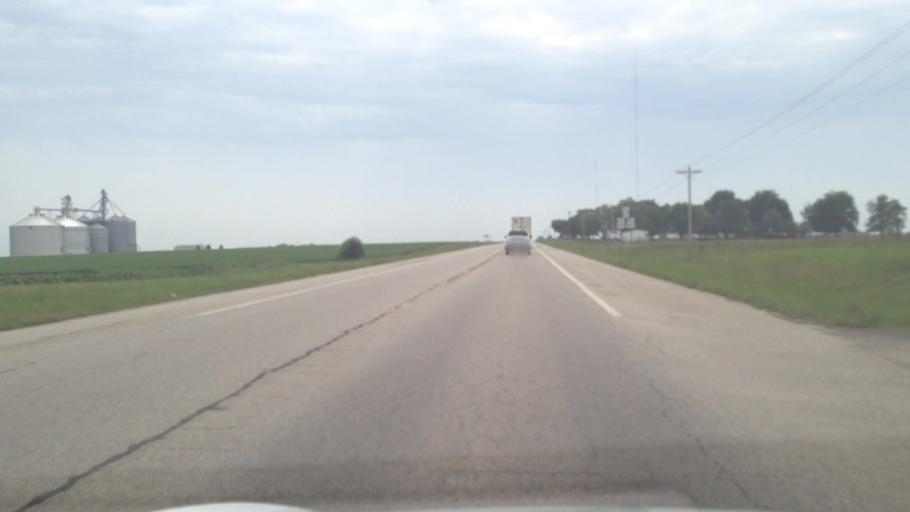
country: US
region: Missouri
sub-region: Jasper County
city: Carl Junction
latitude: 37.2367
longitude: -94.7050
